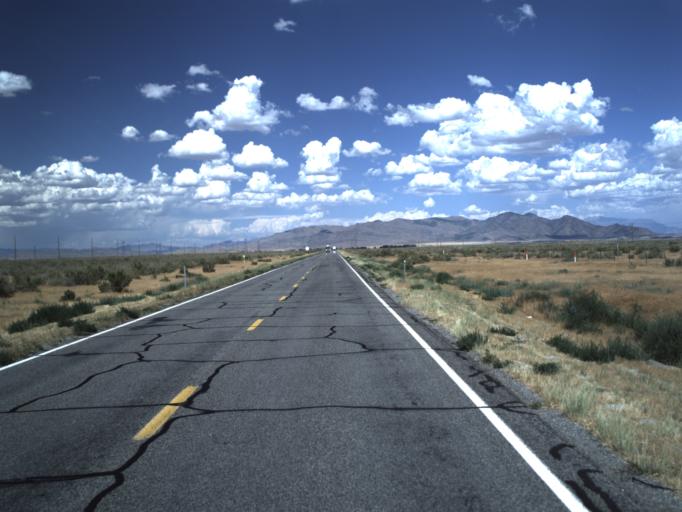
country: US
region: Utah
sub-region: Millard County
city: Delta
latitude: 39.4663
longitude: -112.4284
